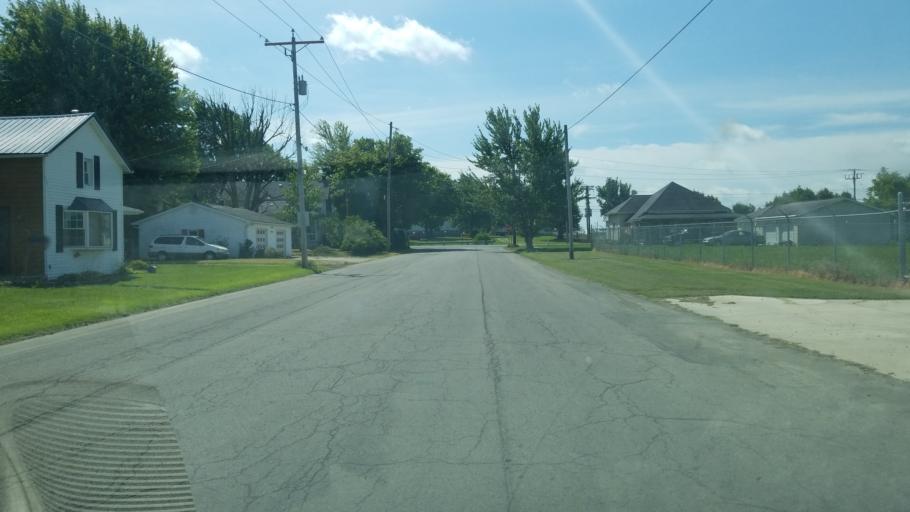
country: US
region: Ohio
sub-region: Hardin County
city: Kenton
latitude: 40.6345
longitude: -83.6081
